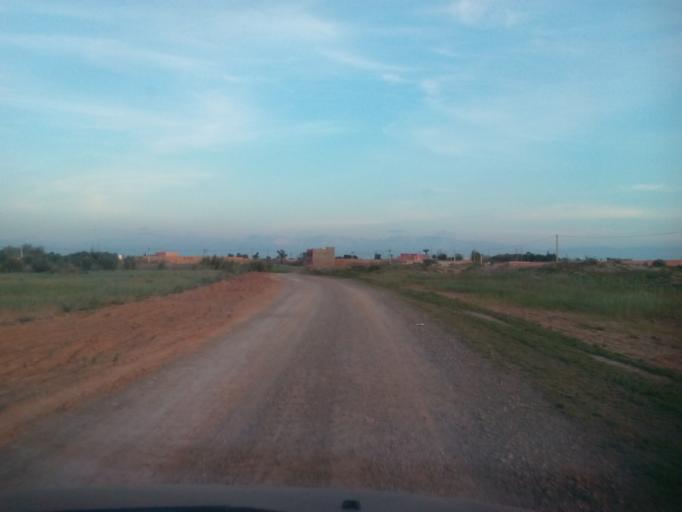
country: MA
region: Marrakech-Tensift-Al Haouz
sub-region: Marrakech
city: Marrakesh
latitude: 31.6294
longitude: -8.2887
